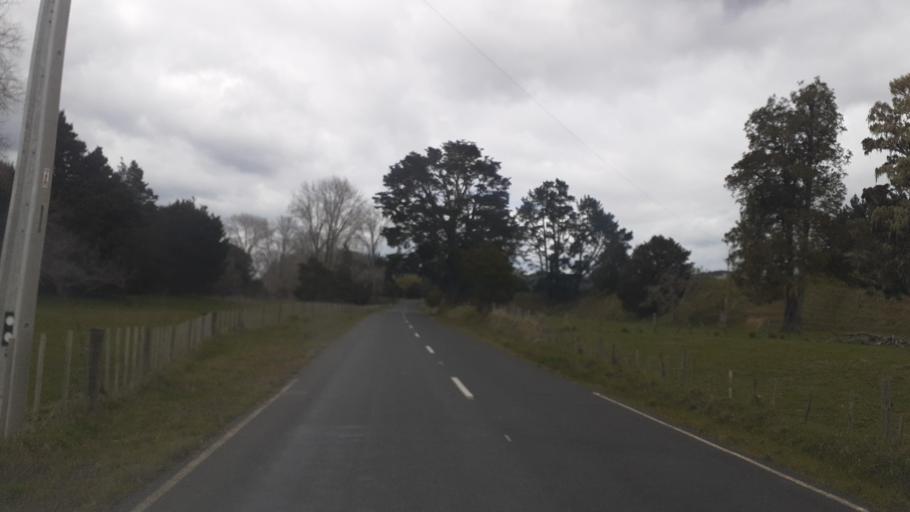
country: NZ
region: Northland
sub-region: Far North District
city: Moerewa
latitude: -35.5814
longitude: 173.9717
